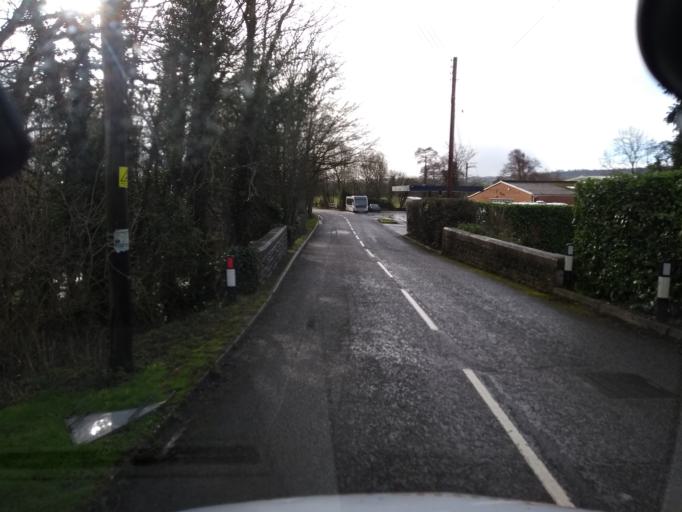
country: GB
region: England
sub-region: Somerset
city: Creech Saint Michael
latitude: 50.9707
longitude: -2.9988
